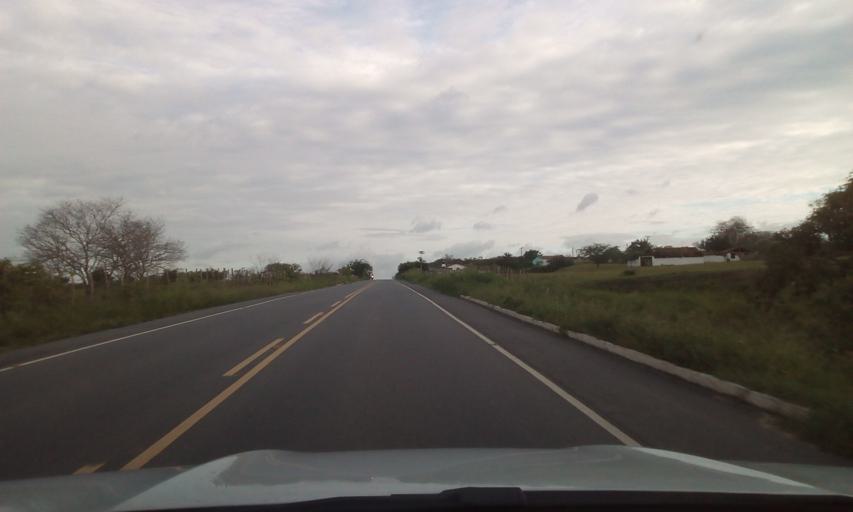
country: BR
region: Paraiba
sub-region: Serra Redonda
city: Alagoa Grande
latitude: -7.2083
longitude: -35.5922
